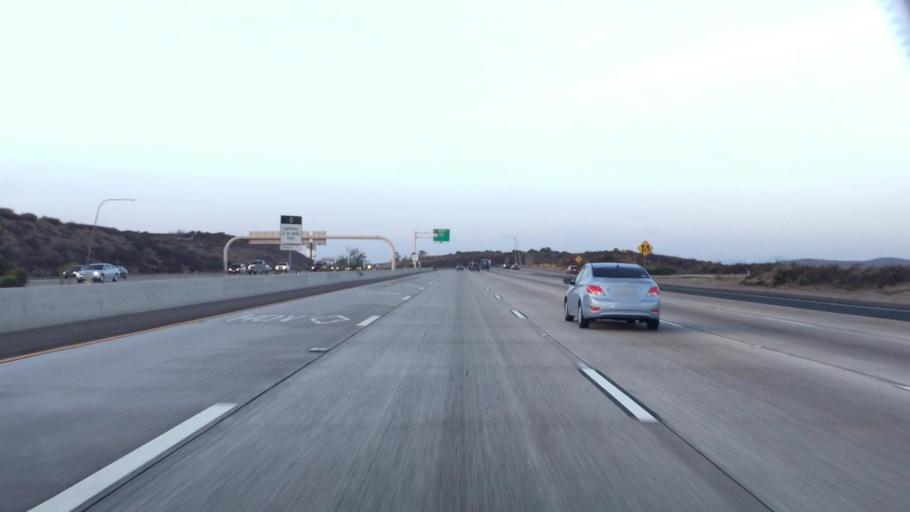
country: US
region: California
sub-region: San Diego County
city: La Mesa
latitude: 32.8447
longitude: -117.1190
